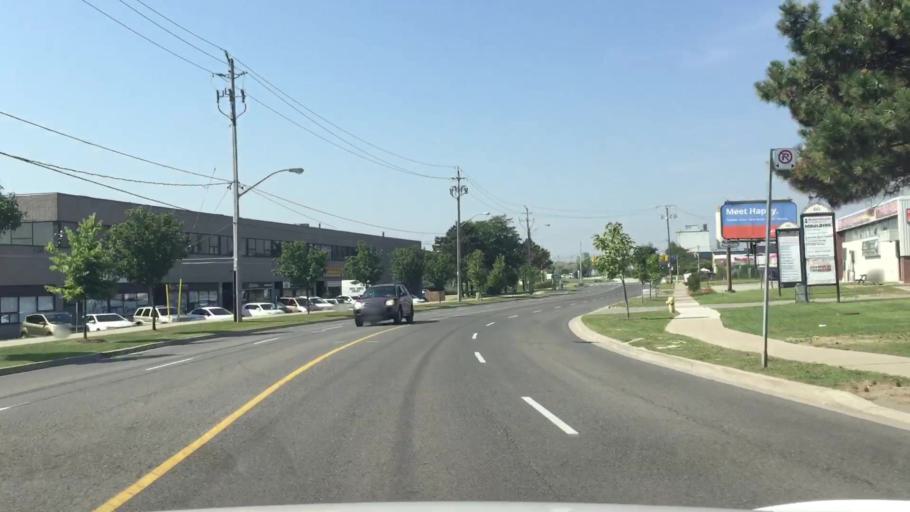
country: CA
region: Ontario
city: Scarborough
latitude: 43.7927
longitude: -79.2574
